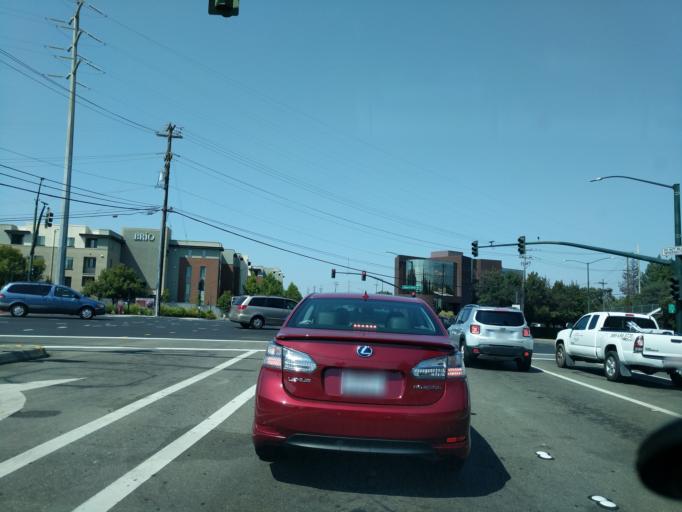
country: US
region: California
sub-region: Contra Costa County
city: Walnut Creek
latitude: 37.9064
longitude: -122.0589
